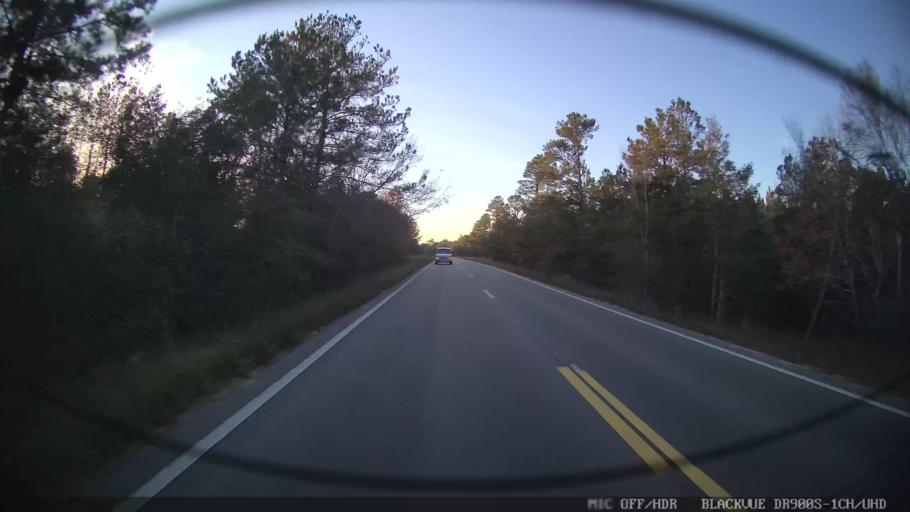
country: US
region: Mississippi
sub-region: Lamar County
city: Lumberton
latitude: 30.9996
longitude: -89.3039
